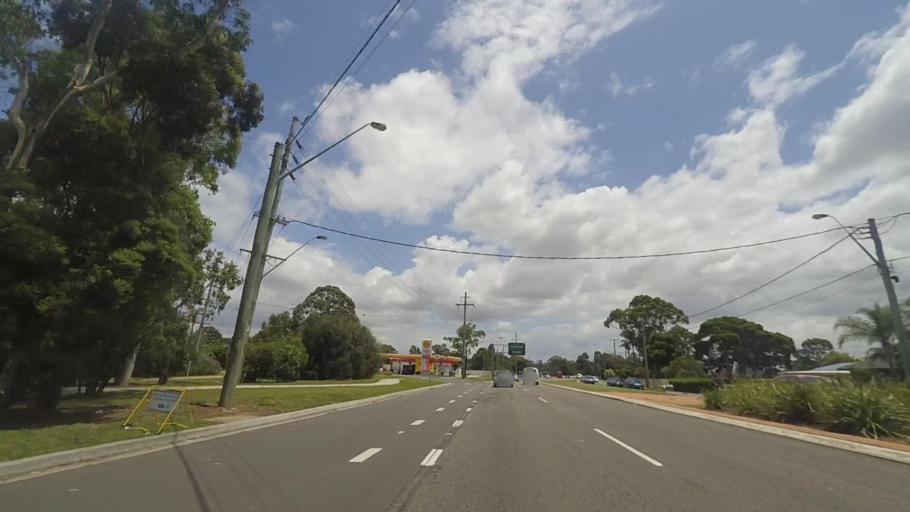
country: AU
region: New South Wales
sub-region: Bankstown
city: Milperra
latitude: -33.9473
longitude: 150.9481
